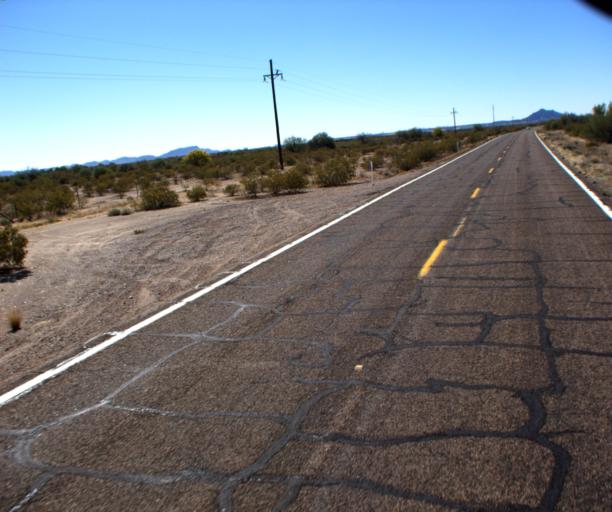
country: US
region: Arizona
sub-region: Pima County
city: Ajo
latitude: 32.4610
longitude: -112.8732
